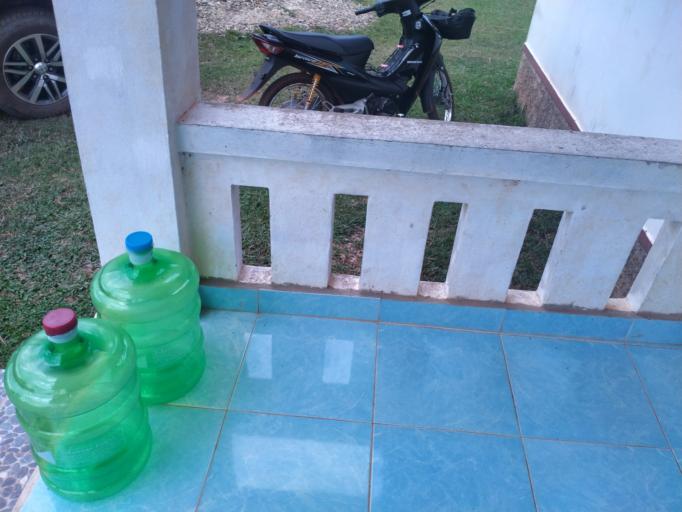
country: TH
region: Changwat Bueng Kan
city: Pak Khat
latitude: 18.5572
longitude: 103.0274
